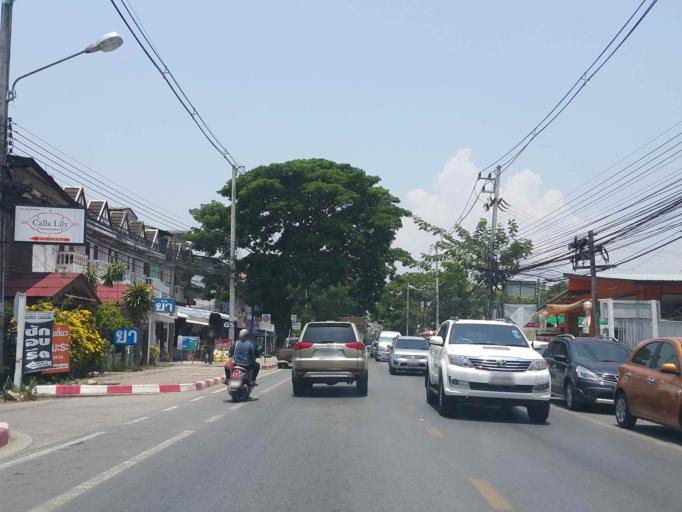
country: TH
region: Chiang Mai
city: Chiang Mai
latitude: 18.7813
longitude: 99.0375
